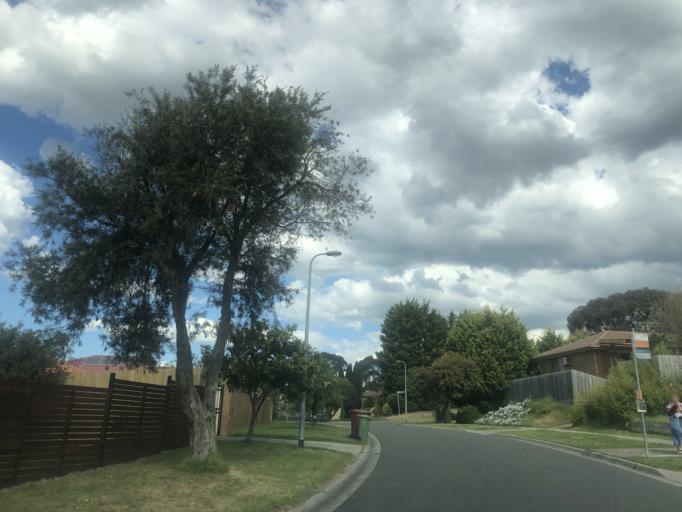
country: AU
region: Victoria
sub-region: Casey
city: Endeavour Hills
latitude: -37.9645
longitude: 145.2695
